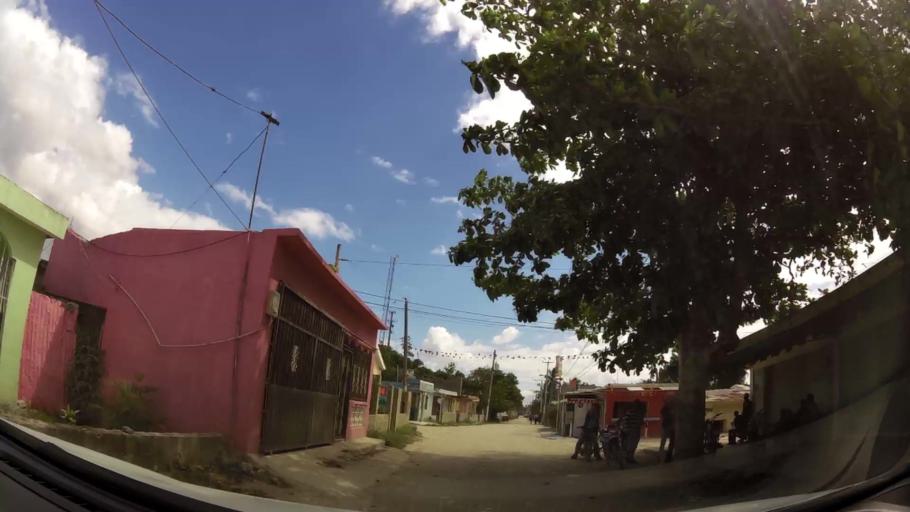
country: DO
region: Santo Domingo
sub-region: Santo Domingo
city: Boca Chica
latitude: 18.4533
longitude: -69.6330
